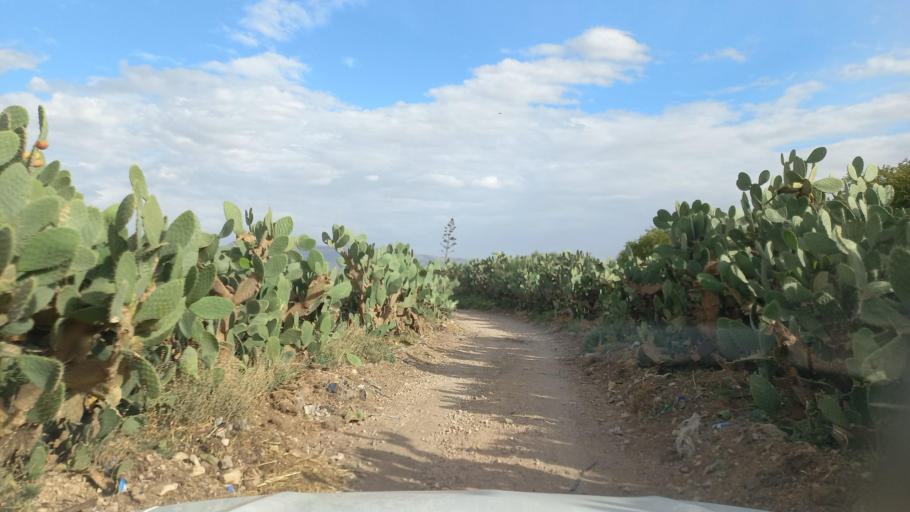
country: TN
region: Al Qasrayn
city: Sbiba
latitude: 35.4505
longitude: 9.0859
